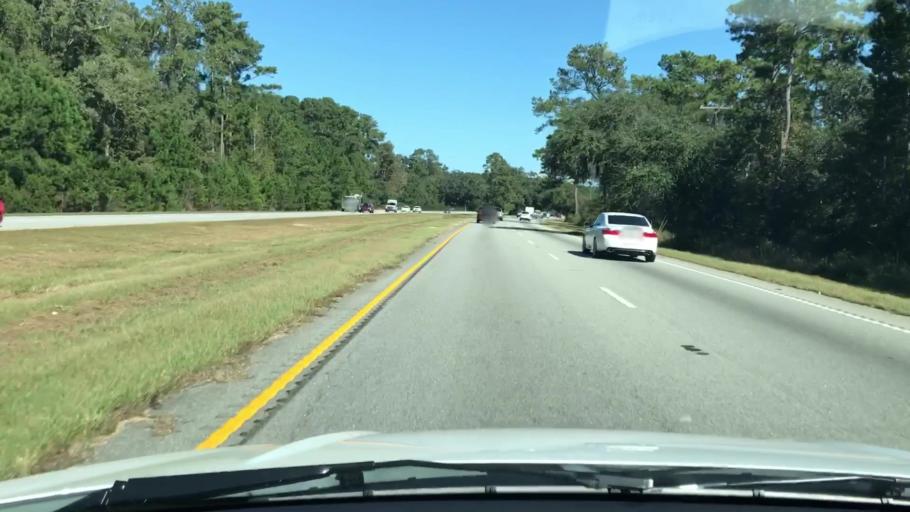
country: US
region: South Carolina
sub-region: Beaufort County
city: Laurel Bay
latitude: 32.3704
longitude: -80.8546
